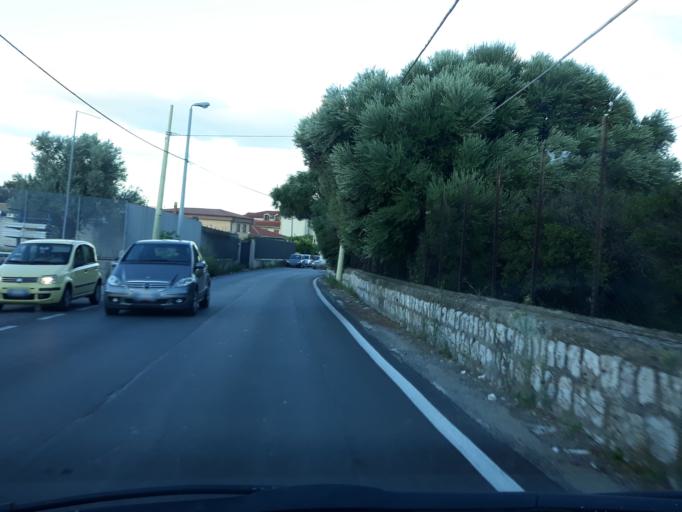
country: IT
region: Sicily
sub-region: Palermo
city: Villa Ciambra
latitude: 38.0857
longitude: 13.3270
